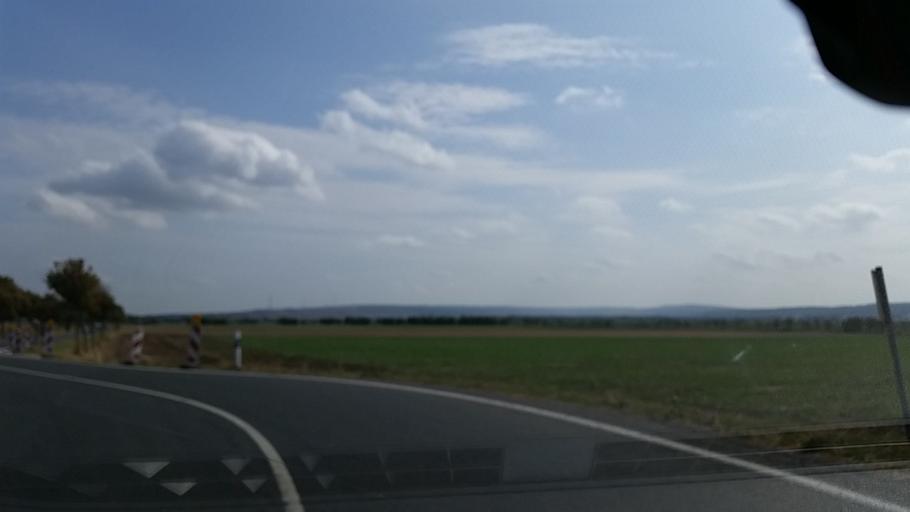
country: DE
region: Thuringia
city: Oldisleben
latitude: 51.3501
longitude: 11.1469
